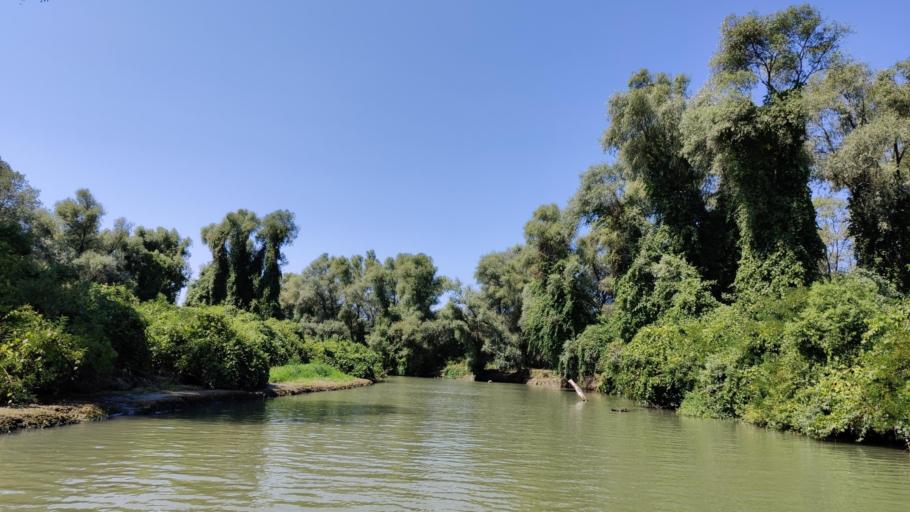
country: RO
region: Tulcea
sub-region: Comuna Pardina
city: Pardina
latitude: 45.2555
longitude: 28.9418
